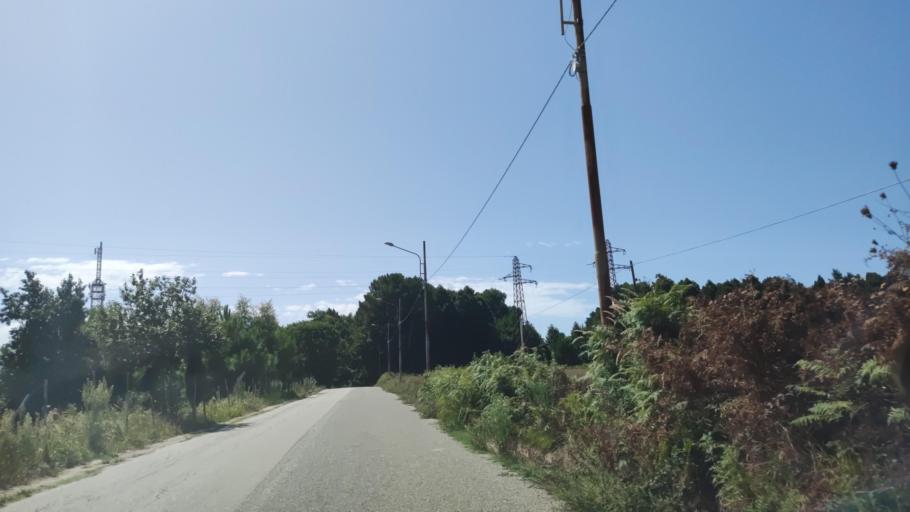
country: IT
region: Calabria
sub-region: Provincia di Reggio Calabria
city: Seminara
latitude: 38.3433
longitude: 15.8438
